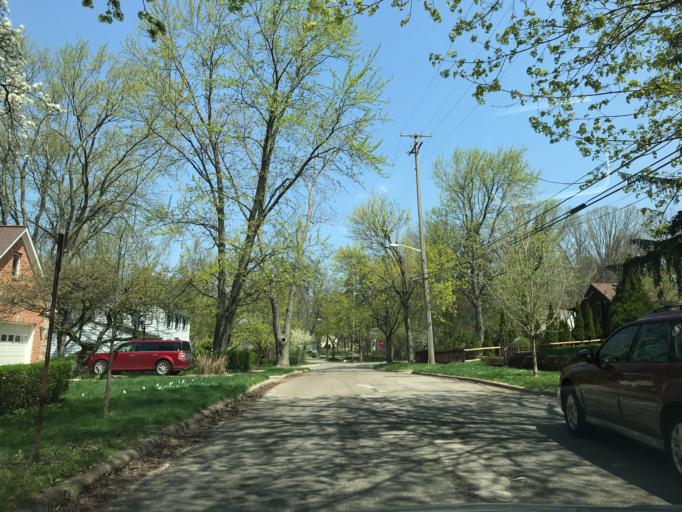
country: US
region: Michigan
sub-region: Washtenaw County
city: Ann Arbor
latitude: 42.2552
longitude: -83.7241
